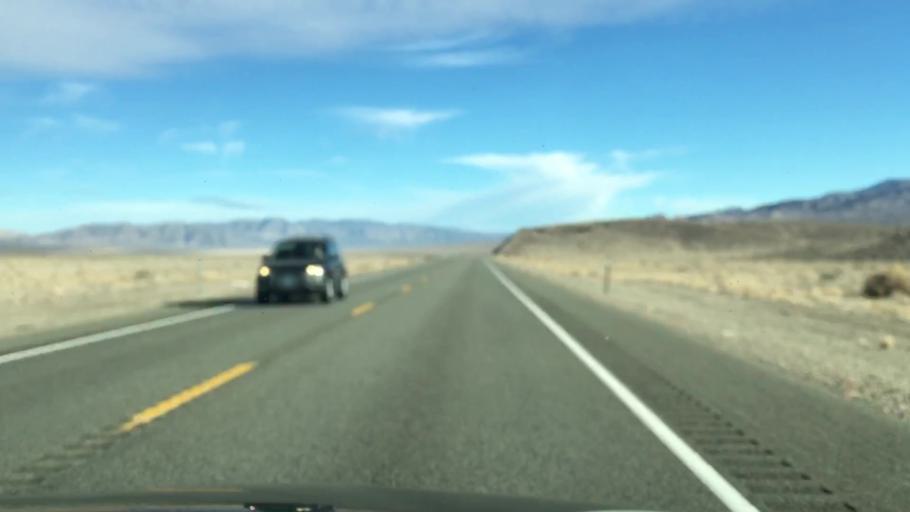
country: US
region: Nevada
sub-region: Mineral County
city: Hawthorne
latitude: 38.5462
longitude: -118.4145
